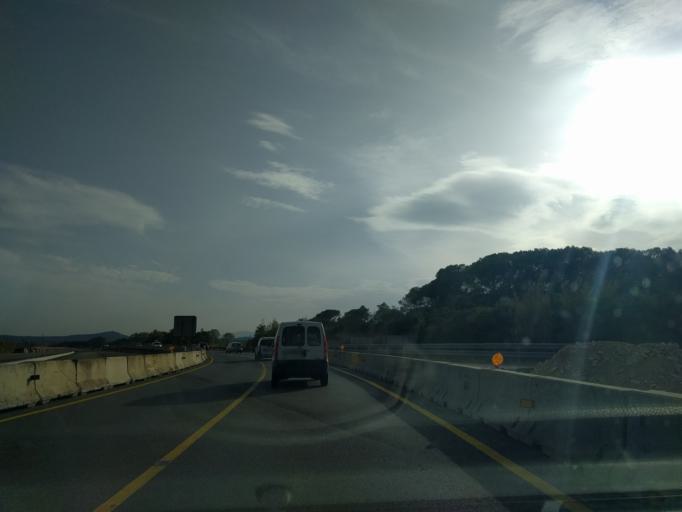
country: ES
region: Catalonia
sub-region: Provincia de Girona
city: Sils
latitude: 41.7998
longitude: 2.7616
